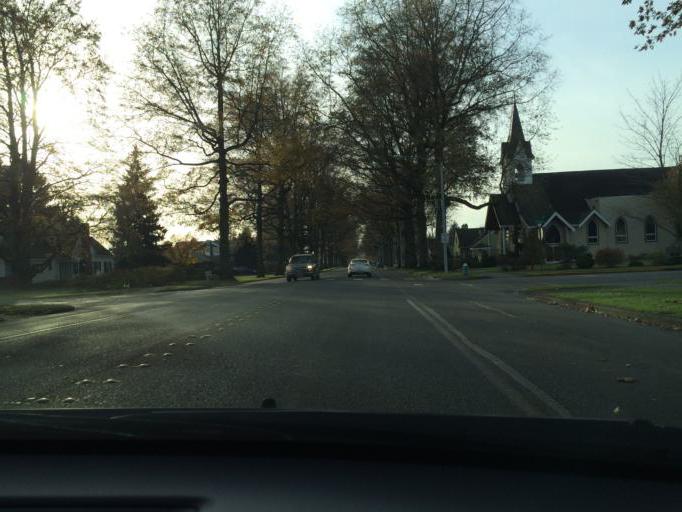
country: US
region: Washington
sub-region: Whatcom County
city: Lynden
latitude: 48.9410
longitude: -122.4588
